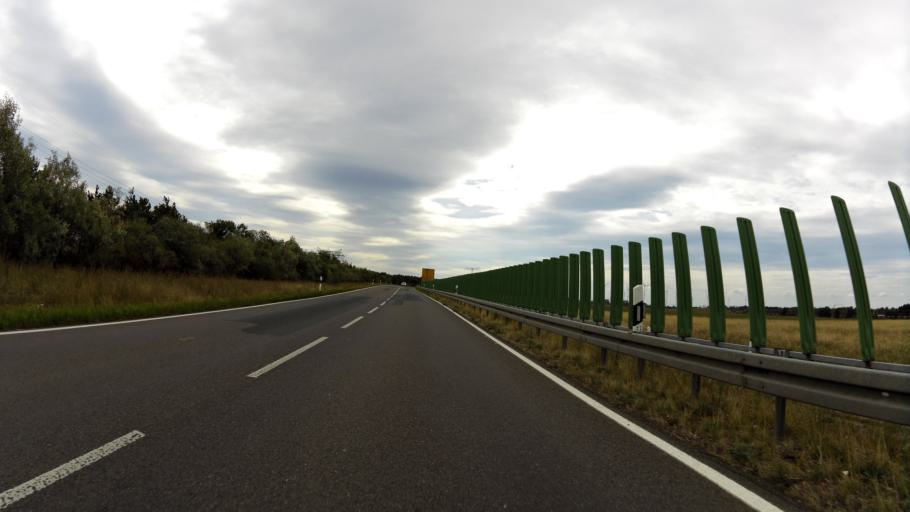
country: DE
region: Brandenburg
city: Heinersbruck
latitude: 51.8111
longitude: 14.5058
